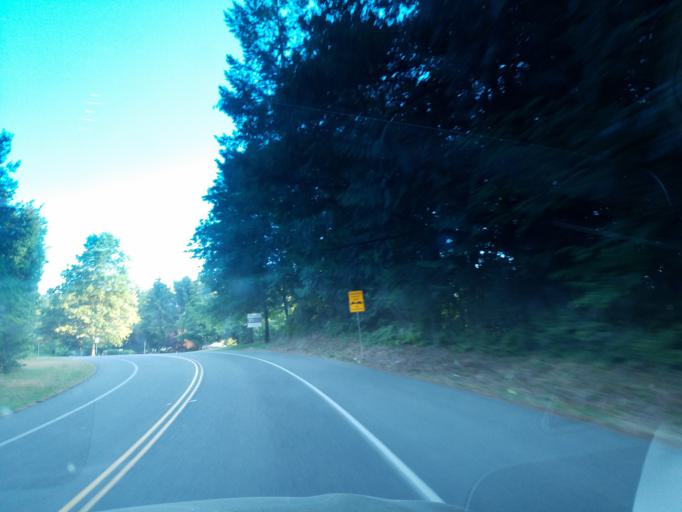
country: US
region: Washington
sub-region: King County
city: City of Sammamish
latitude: 47.6380
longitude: -122.0141
